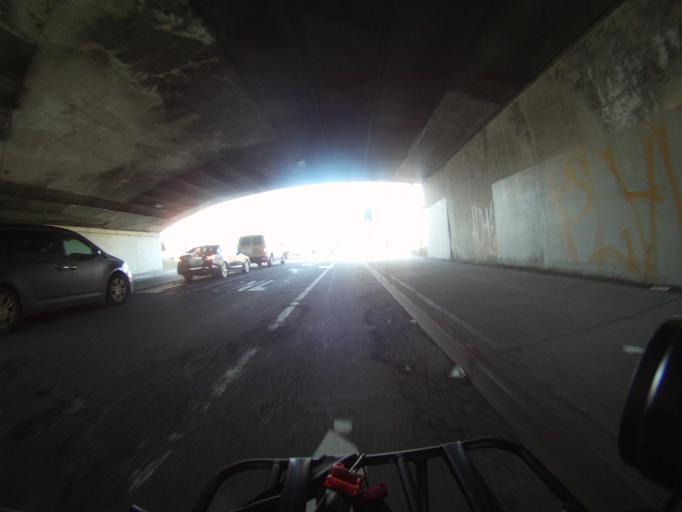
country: US
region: New York
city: New York City
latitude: 40.6982
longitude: -73.9622
